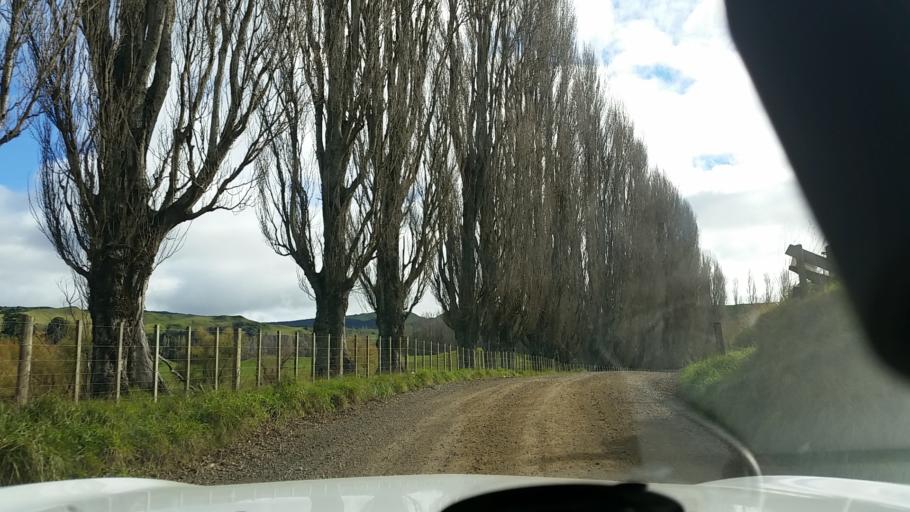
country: NZ
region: Hawke's Bay
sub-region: Napier City
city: Napier
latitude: -39.1039
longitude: 176.8825
